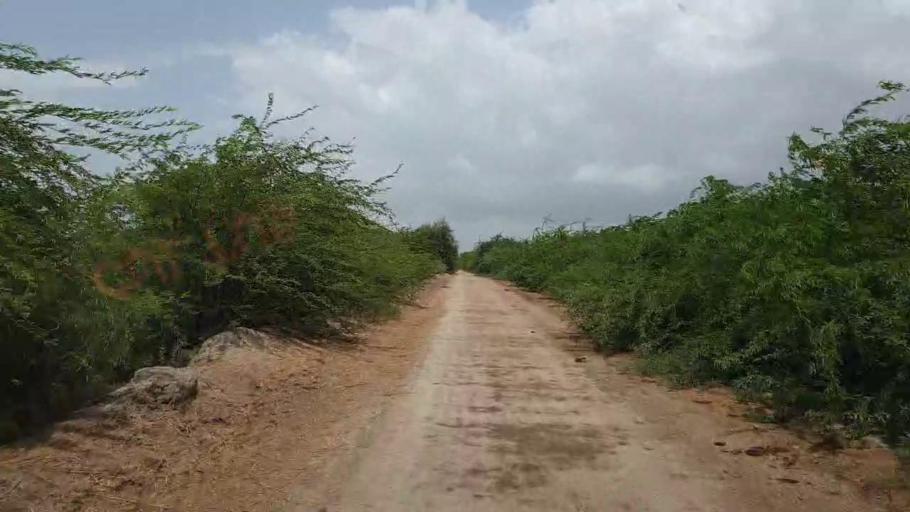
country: PK
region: Sindh
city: Kario
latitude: 24.6953
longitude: 68.6455
